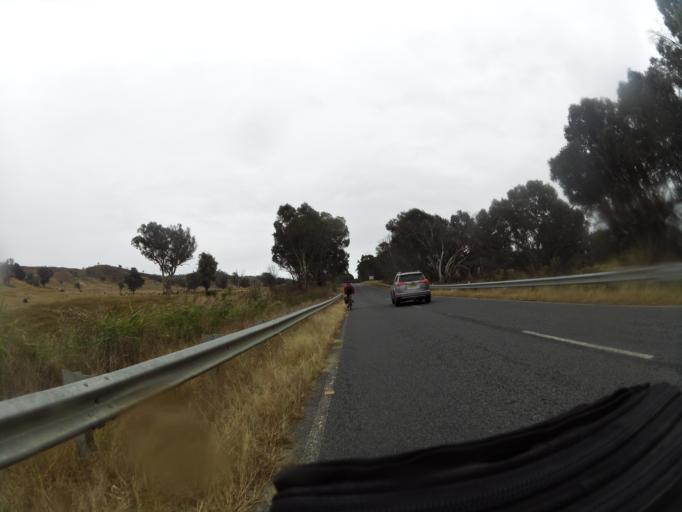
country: AU
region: New South Wales
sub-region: Greater Hume Shire
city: Holbrook
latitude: -36.2155
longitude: 147.8278
